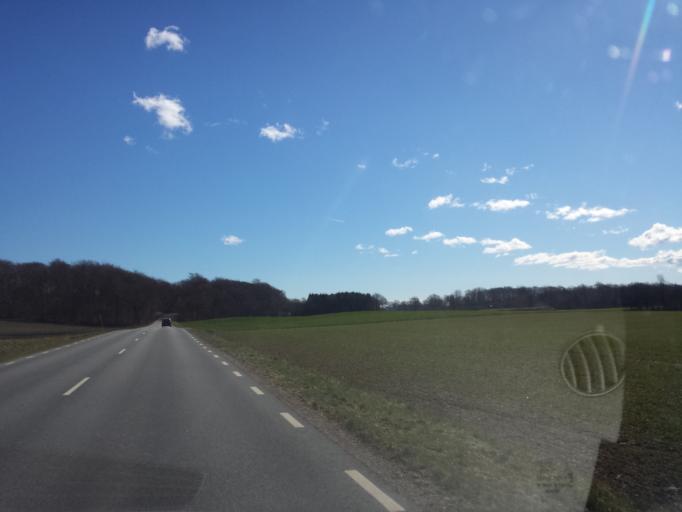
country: SE
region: Skane
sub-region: Tomelilla Kommun
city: Tomelilla
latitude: 55.6544
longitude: 13.9261
